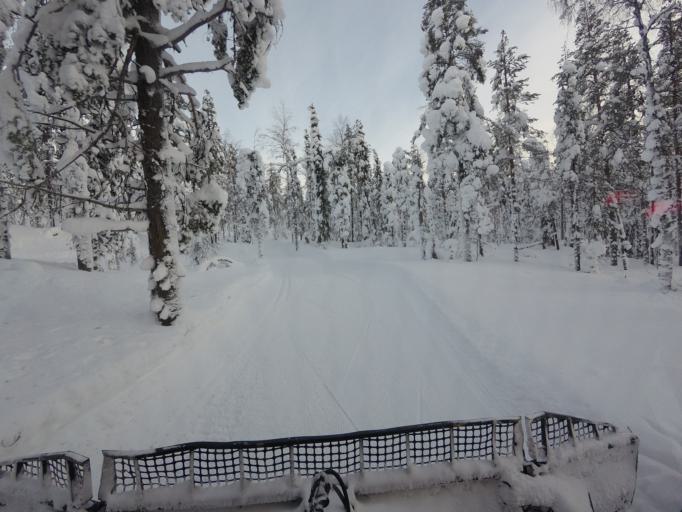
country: FI
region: Lapland
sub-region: Tunturi-Lappi
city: Kolari
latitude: 67.6484
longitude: 24.2386
